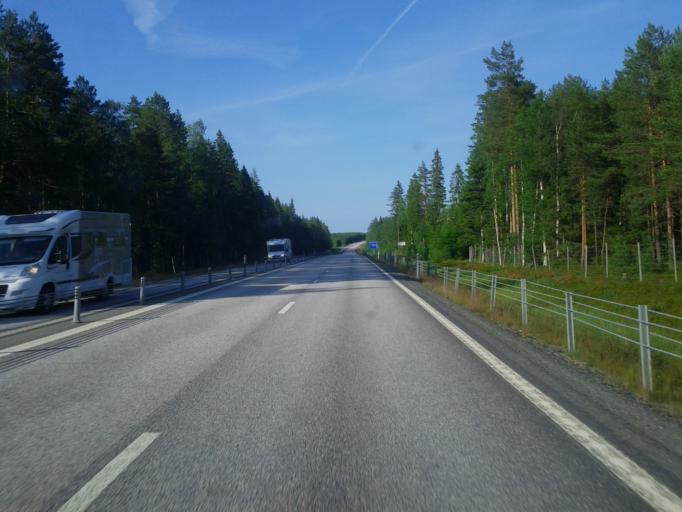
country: SE
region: Vaesterbotten
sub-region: Umea Kommun
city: Saevar
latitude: 63.9774
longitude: 20.7218
